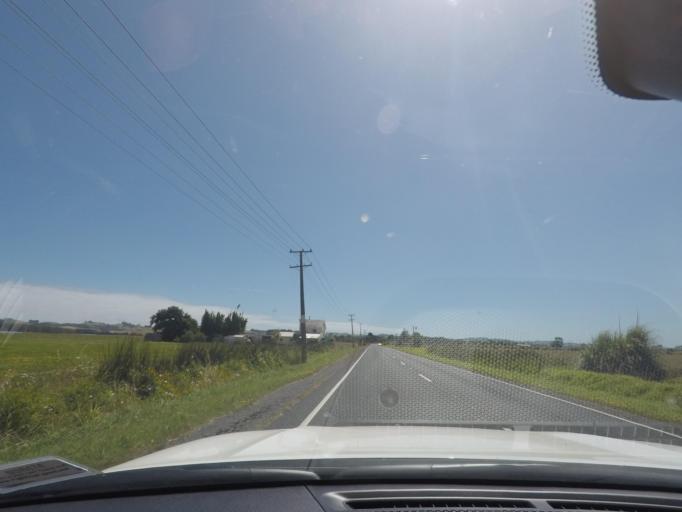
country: NZ
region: Auckland
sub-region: Auckland
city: Parakai
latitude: -36.6509
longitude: 174.4193
